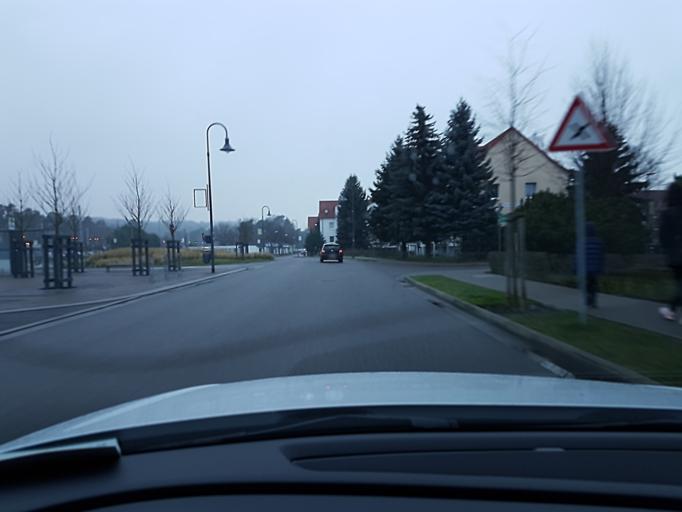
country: DE
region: Mecklenburg-Vorpommern
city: Ostseebad Binz
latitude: 54.4050
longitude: 13.6018
